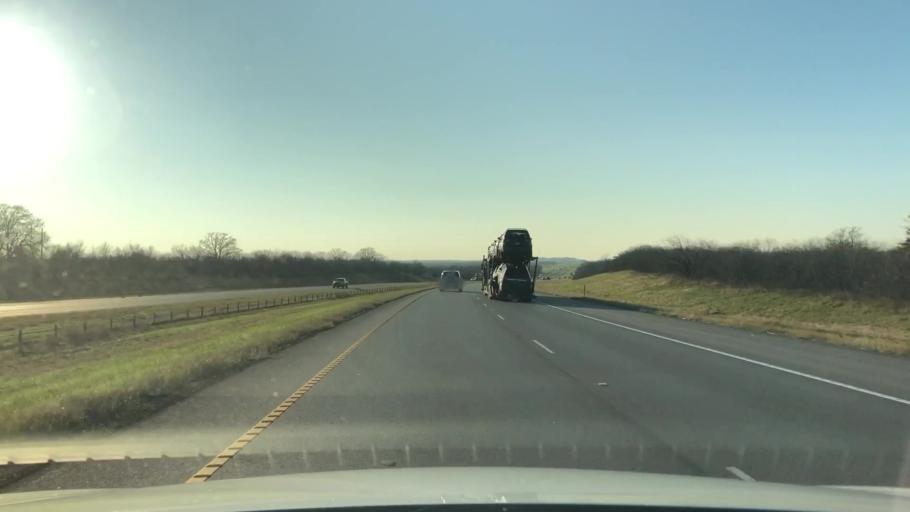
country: US
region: Texas
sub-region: Gonzales County
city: Gonzales
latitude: 29.6496
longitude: -97.4864
